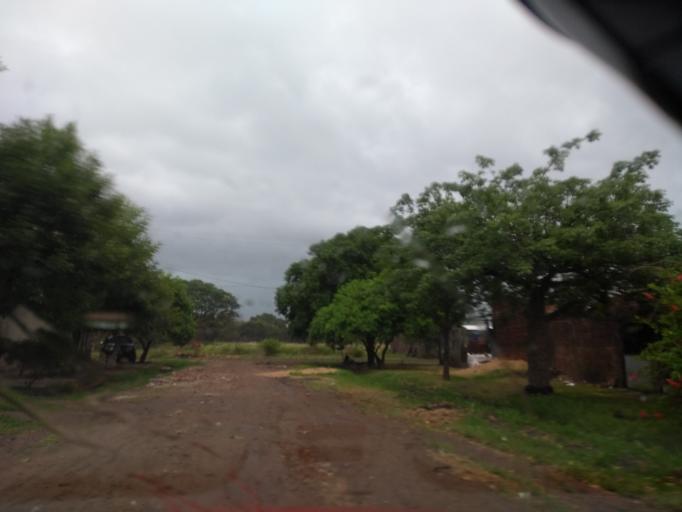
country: AR
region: Chaco
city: Fontana
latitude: -27.4219
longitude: -59.0475
